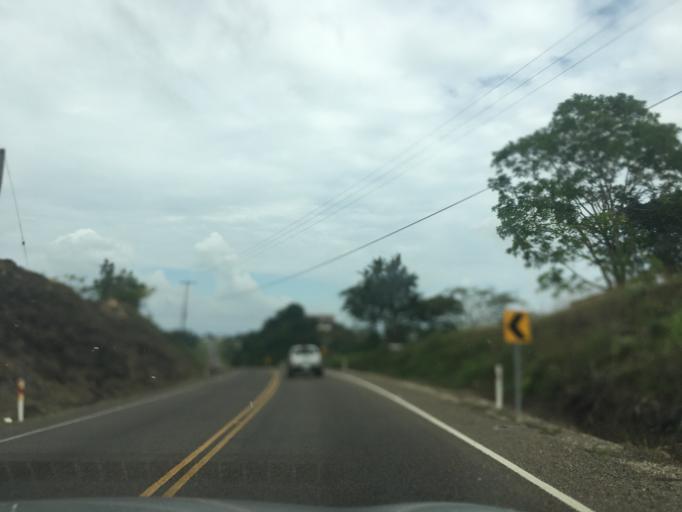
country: BZ
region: Cayo
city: Belmopan
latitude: 17.2296
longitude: -88.7794
